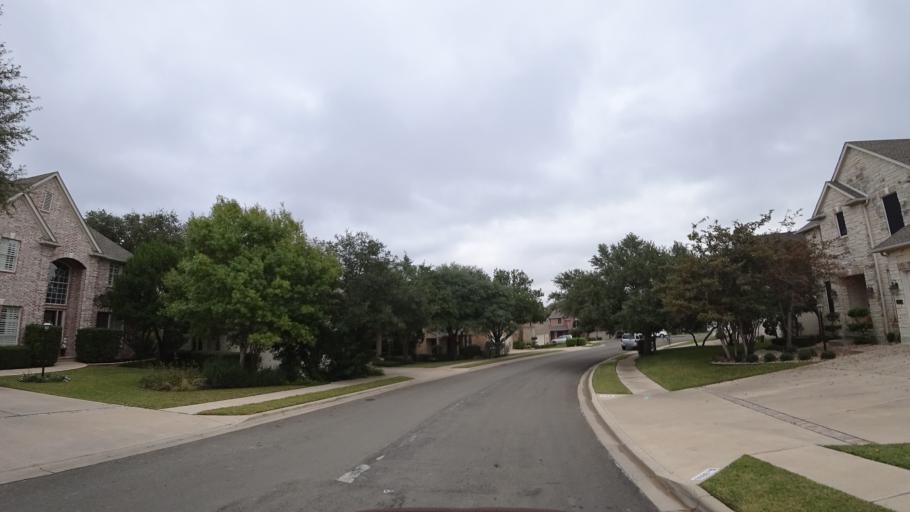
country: US
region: Texas
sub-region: Williamson County
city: Anderson Mill
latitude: 30.4320
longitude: -97.8312
